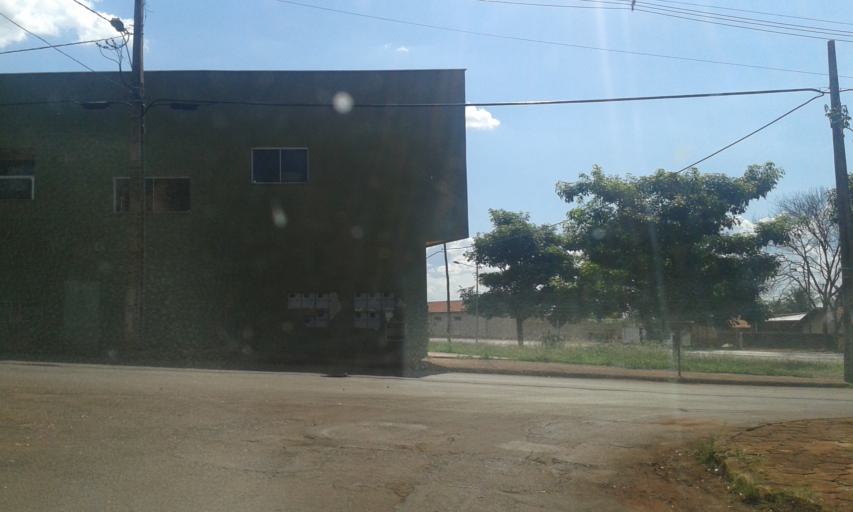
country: BR
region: Minas Gerais
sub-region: Capinopolis
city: Capinopolis
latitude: -18.6867
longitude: -49.5737
